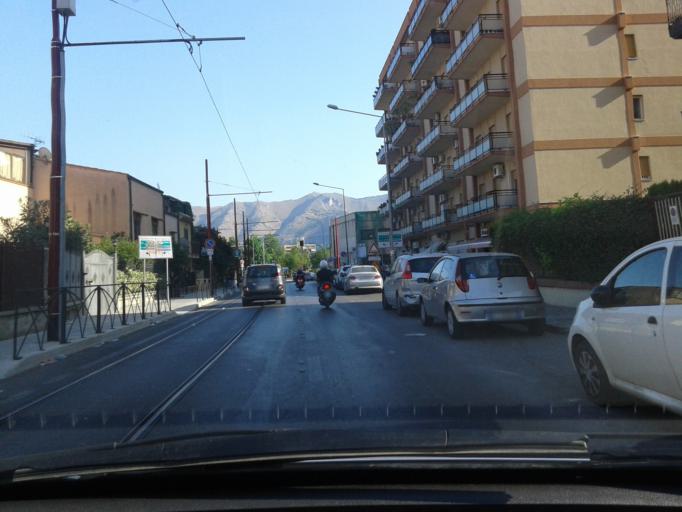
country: IT
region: Sicily
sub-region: Palermo
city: Palermo
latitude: 38.1040
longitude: 13.3296
